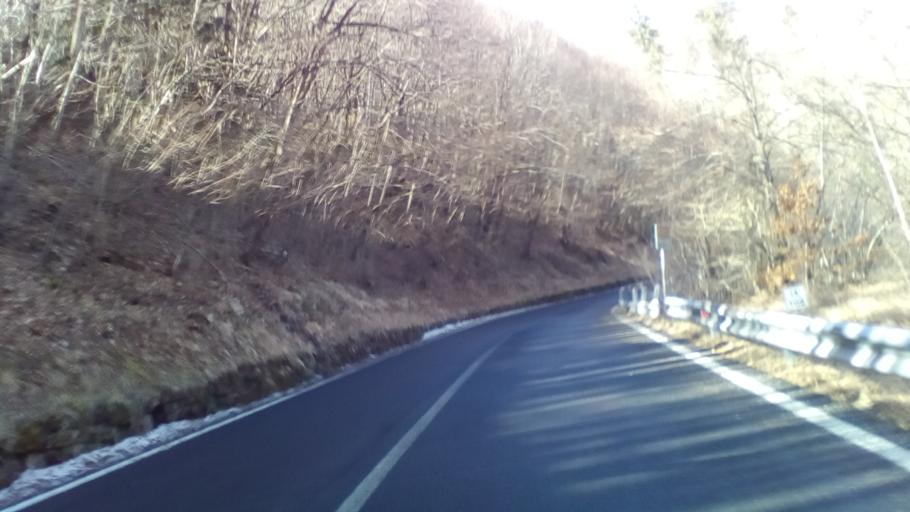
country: IT
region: Emilia-Romagna
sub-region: Provincia di Modena
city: Pievepelago
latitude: 44.2182
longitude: 10.6134
